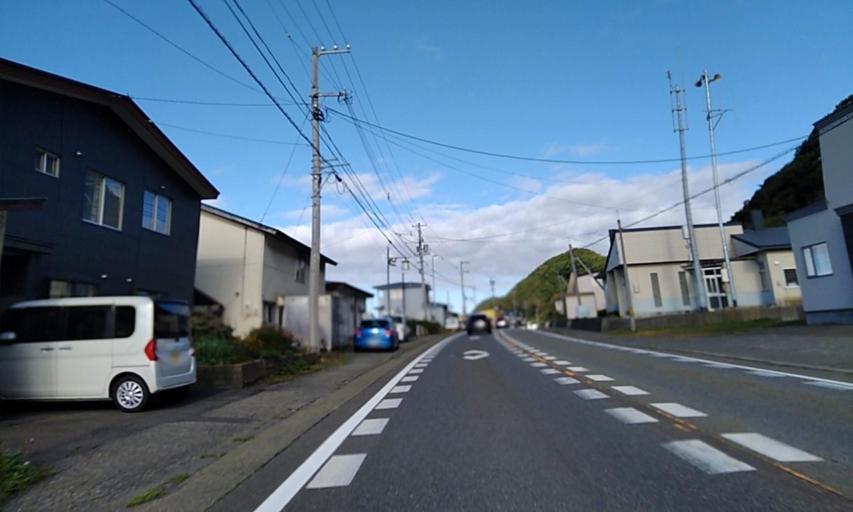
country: JP
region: Hokkaido
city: Shizunai-furukawacho
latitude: 42.2528
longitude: 142.5409
